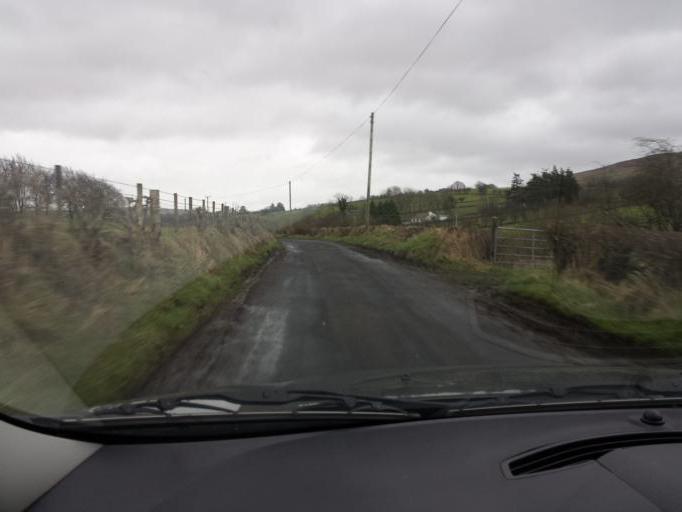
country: GB
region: Northern Ireland
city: Broughshane
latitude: 54.9740
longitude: -6.1983
